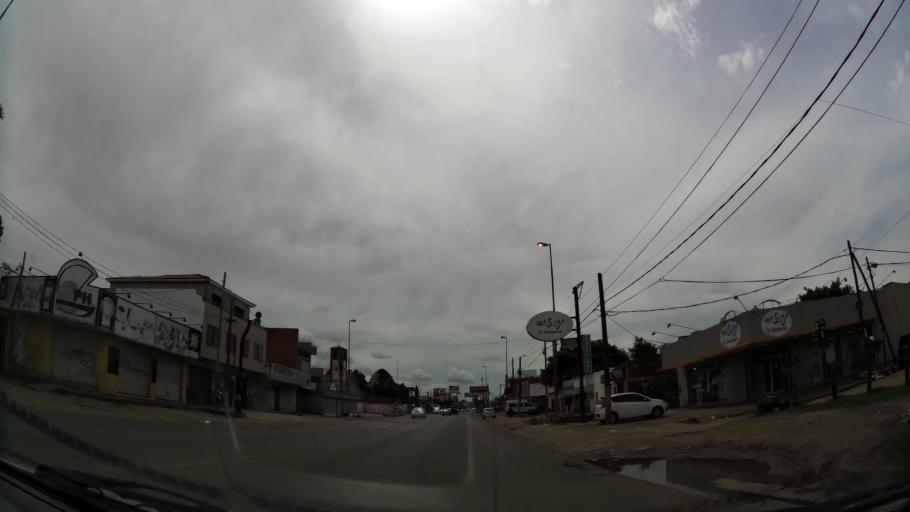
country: AR
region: Buenos Aires
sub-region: Partido de Quilmes
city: Quilmes
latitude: -34.7697
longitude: -58.2708
